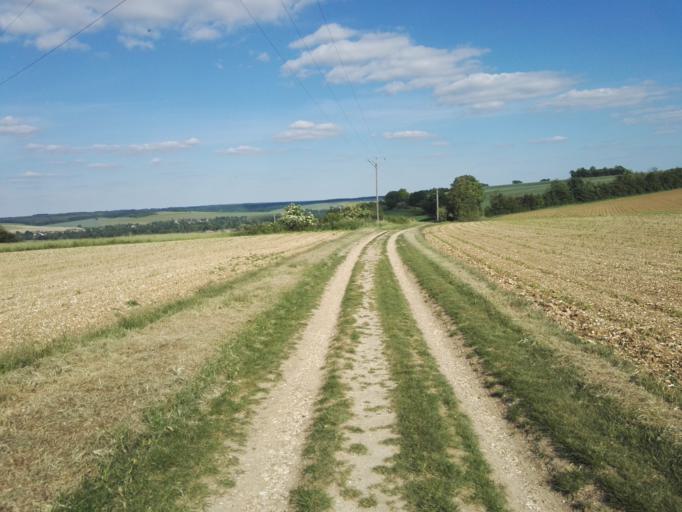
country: FR
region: Haute-Normandie
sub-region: Departement de l'Eure
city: Pacy-sur-Eure
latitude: 48.9884
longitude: 1.3761
